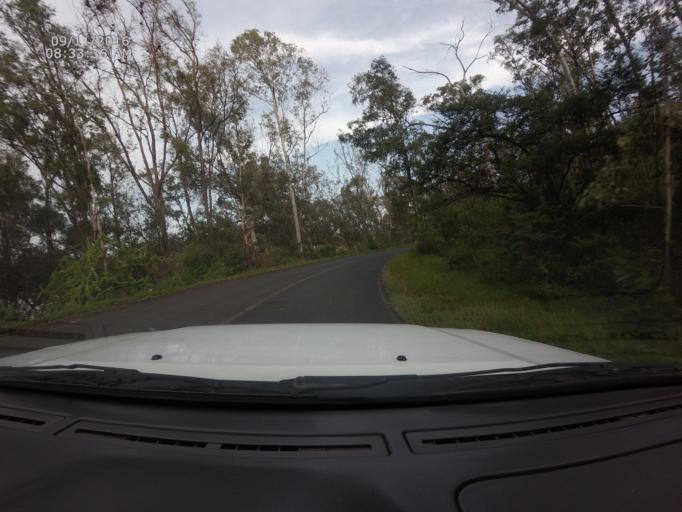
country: MX
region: Michoacan
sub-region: Morelia
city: Morelos
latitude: 19.6283
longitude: -101.2550
